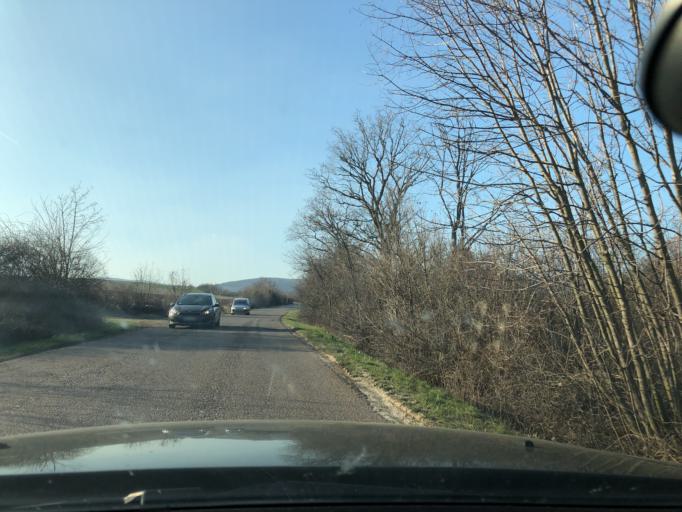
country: HU
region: Nograd
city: Paszto
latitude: 47.9054
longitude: 19.6676
